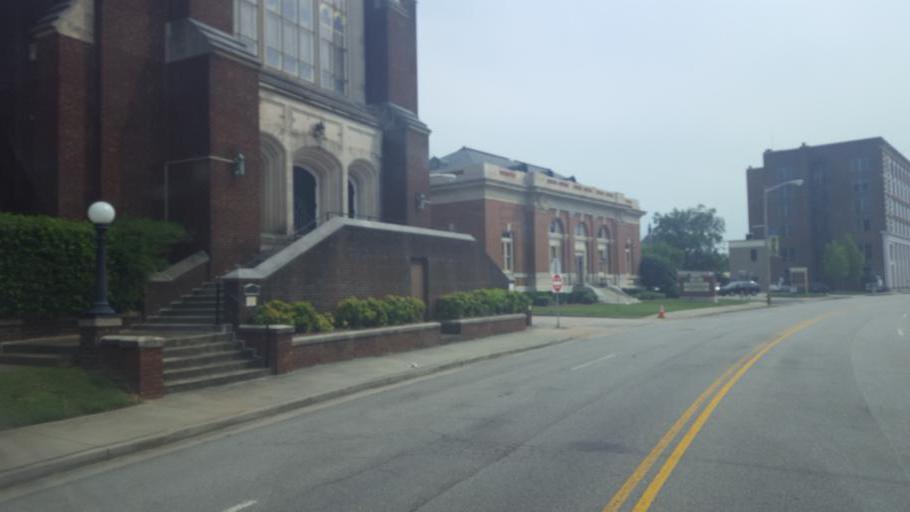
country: US
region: South Carolina
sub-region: York County
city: Rock Hill
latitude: 34.9257
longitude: -81.0244
